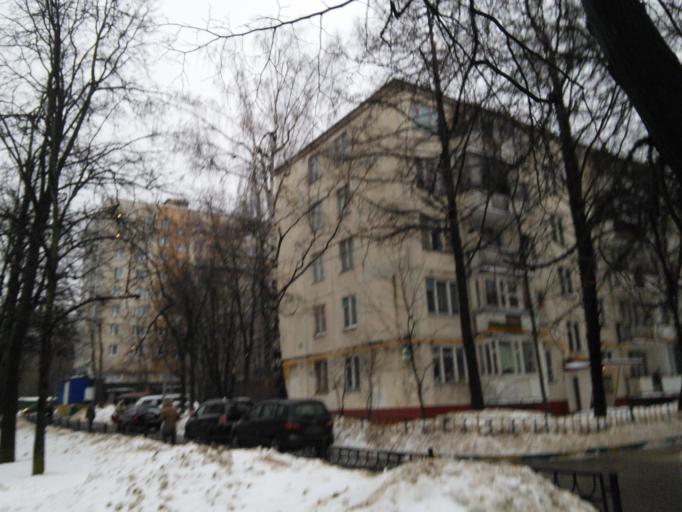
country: RU
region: Moskovskaya
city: Cheremushki
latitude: 55.6475
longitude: 37.5268
